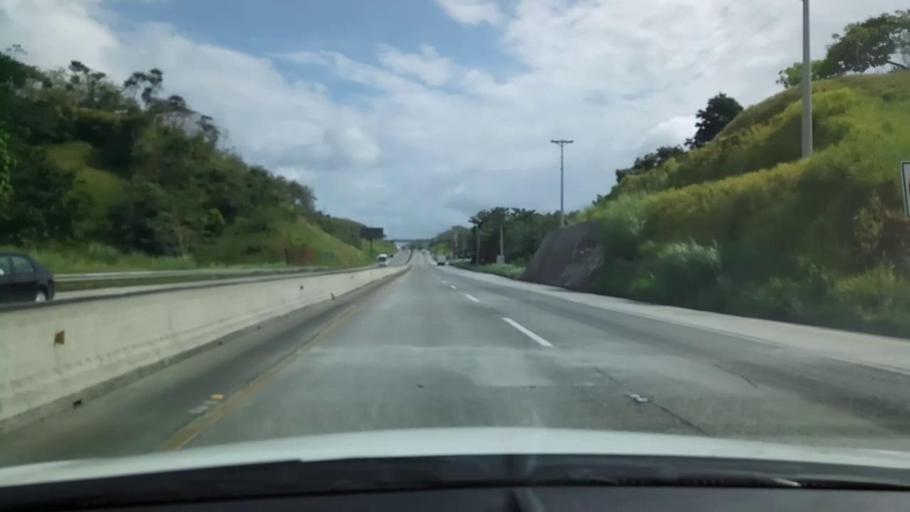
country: PA
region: Colon
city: El Giral
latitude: 9.2509
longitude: -79.6900
